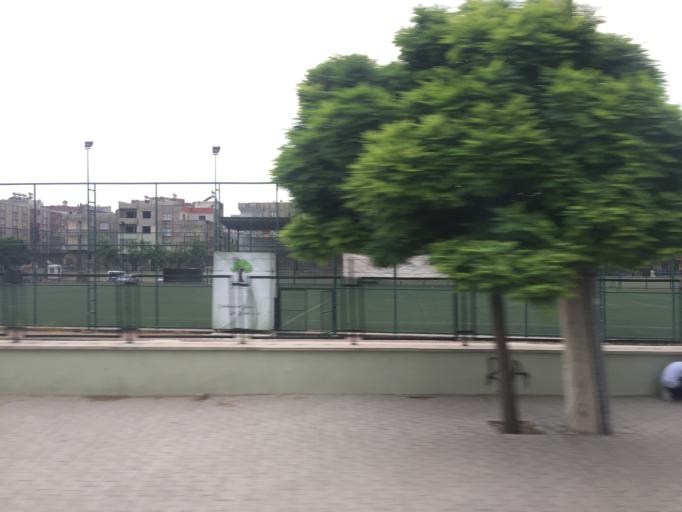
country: TR
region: Gaziantep
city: Gaziantep
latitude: 37.0648
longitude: 37.4149
